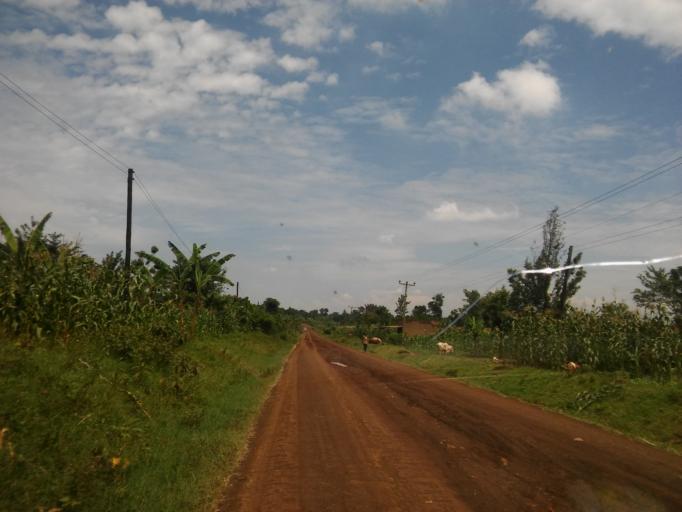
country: UG
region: Eastern Region
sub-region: Bududa District
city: Bududa
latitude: 0.8874
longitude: 34.2608
